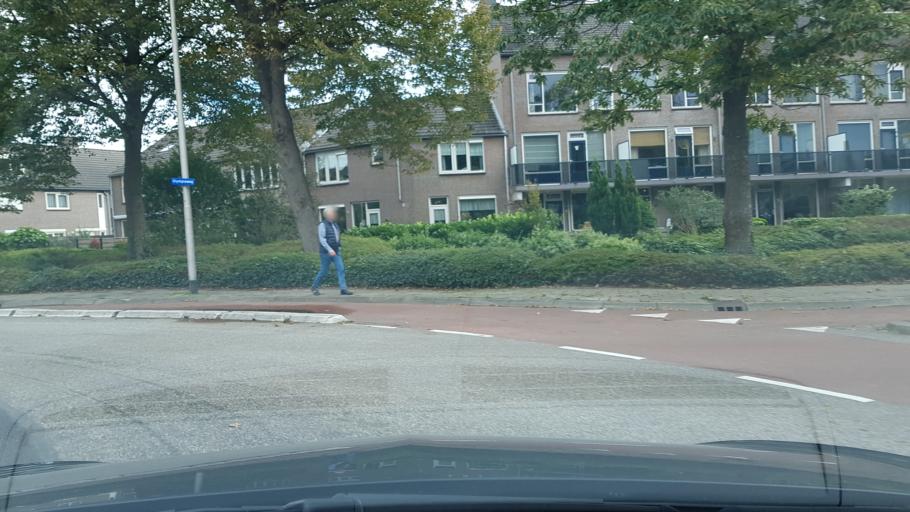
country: NL
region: South Holland
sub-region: Gemeente Hillegom
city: Hillegom
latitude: 52.2855
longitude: 4.5851
